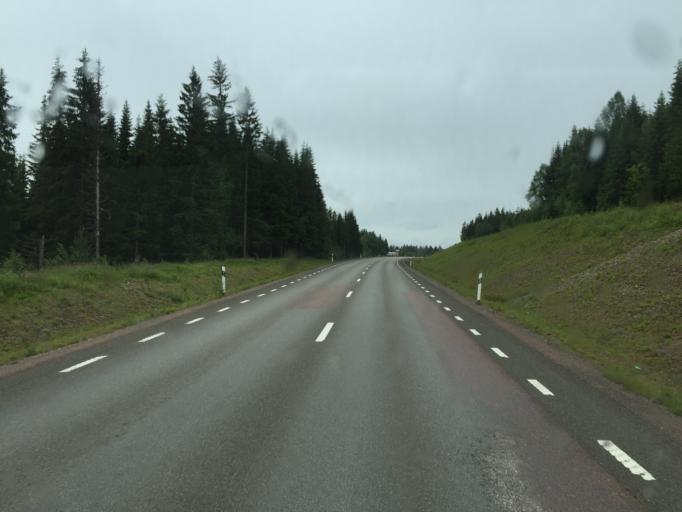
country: SE
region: Dalarna
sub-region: Malung-Saelens kommun
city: Malung
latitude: 60.5768
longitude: 13.5777
